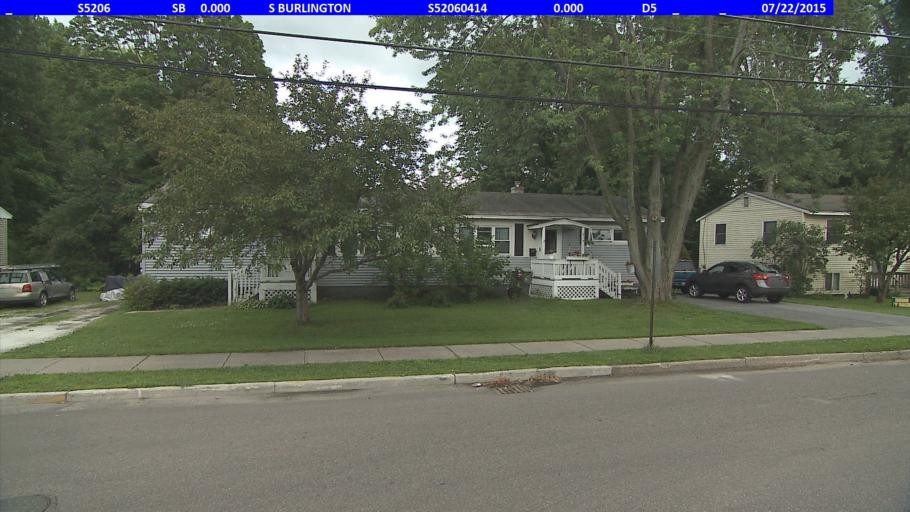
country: US
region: Vermont
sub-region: Chittenden County
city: South Burlington
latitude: 44.4708
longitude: -73.1634
